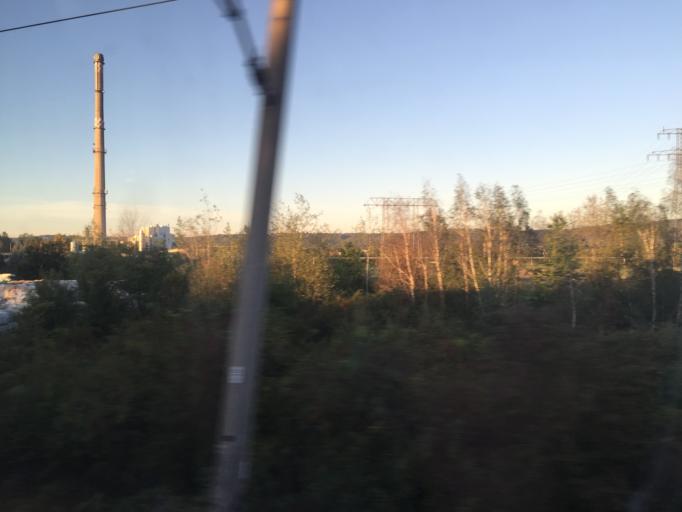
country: DE
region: Saxony
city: Heidenau
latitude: 50.9931
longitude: 13.8392
